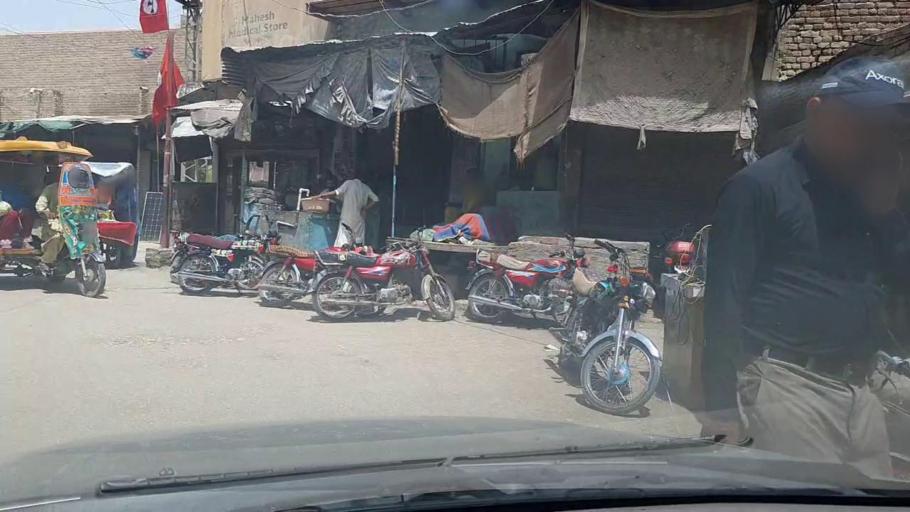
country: PK
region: Sindh
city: Ratodero
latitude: 27.8022
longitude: 68.2870
